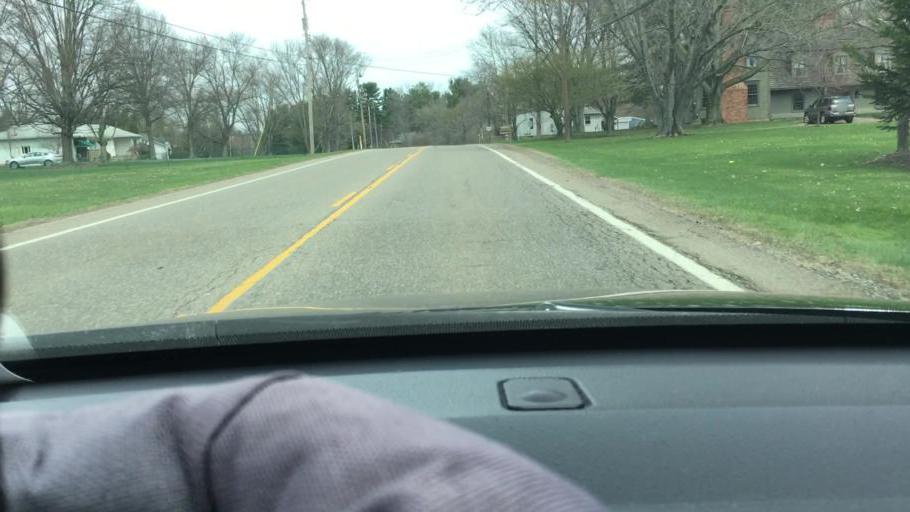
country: US
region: Ohio
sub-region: Columbiana County
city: Columbiana
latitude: 40.9288
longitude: -80.6766
